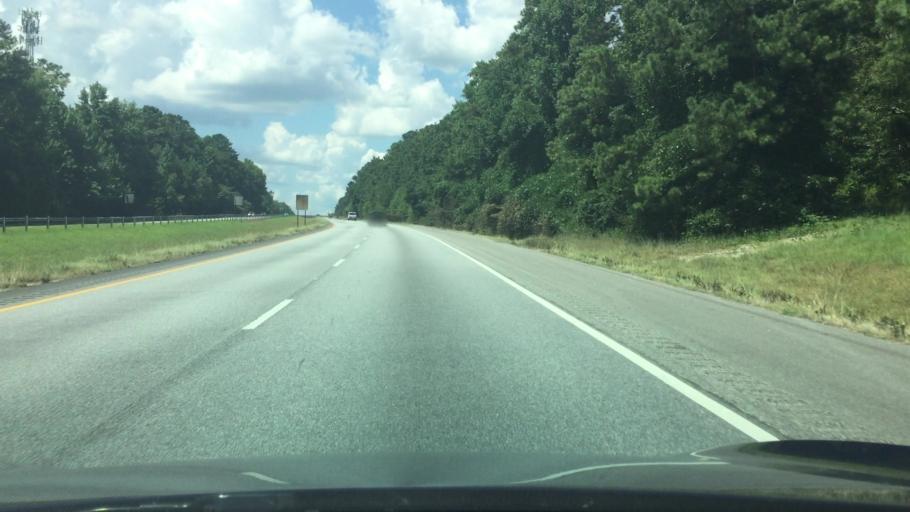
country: US
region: Alabama
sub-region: Lee County
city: Auburn
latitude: 32.5947
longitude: -85.4516
